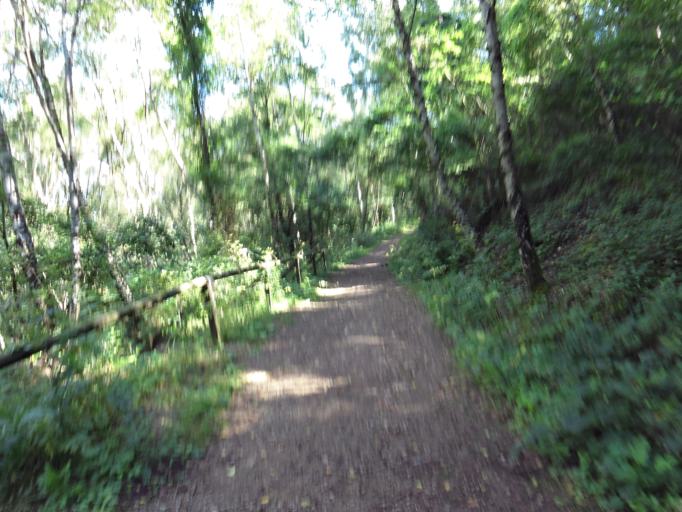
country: DE
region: North Rhine-Westphalia
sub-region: Regierungsbezirk Koln
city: Herzogenrath
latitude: 50.8934
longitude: 6.1109
